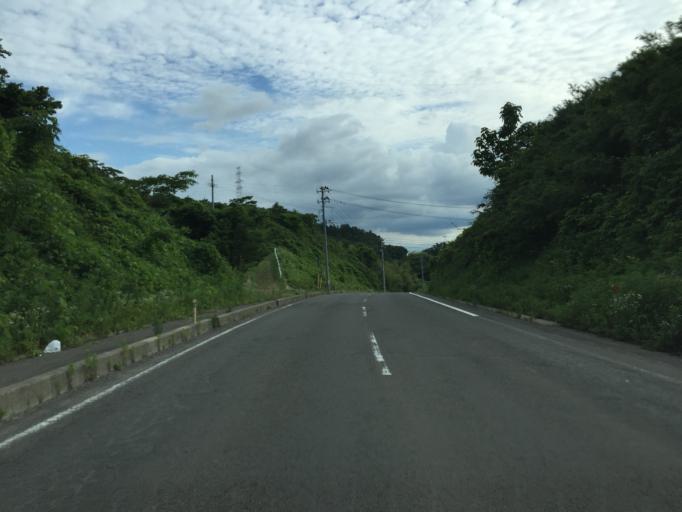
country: JP
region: Fukushima
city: Fukushima-shi
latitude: 37.6943
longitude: 140.5053
